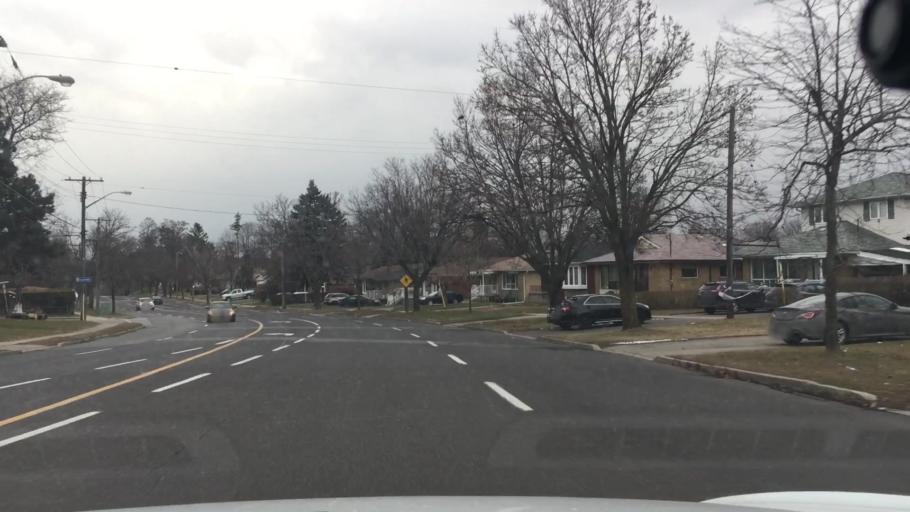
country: CA
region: Ontario
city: Scarborough
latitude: 43.7571
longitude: -79.2353
